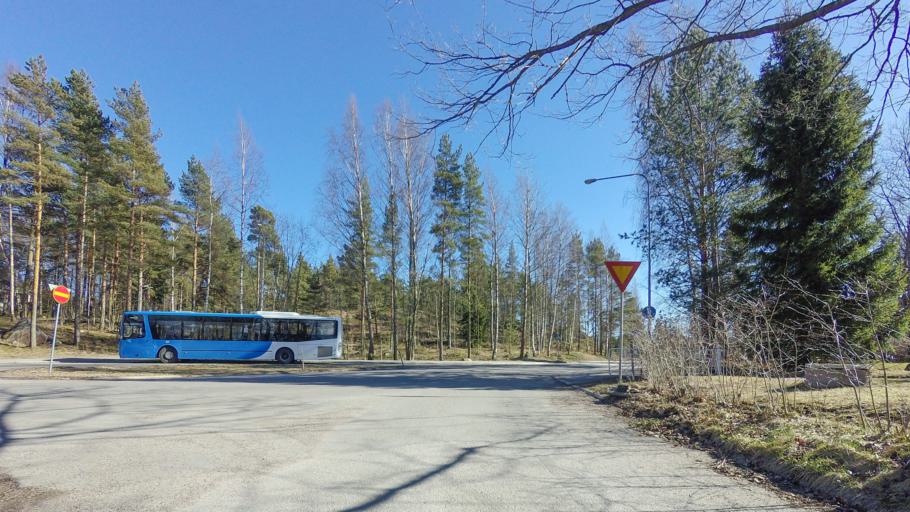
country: FI
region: Uusimaa
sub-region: Helsinki
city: Vantaa
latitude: 60.1707
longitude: 25.0794
